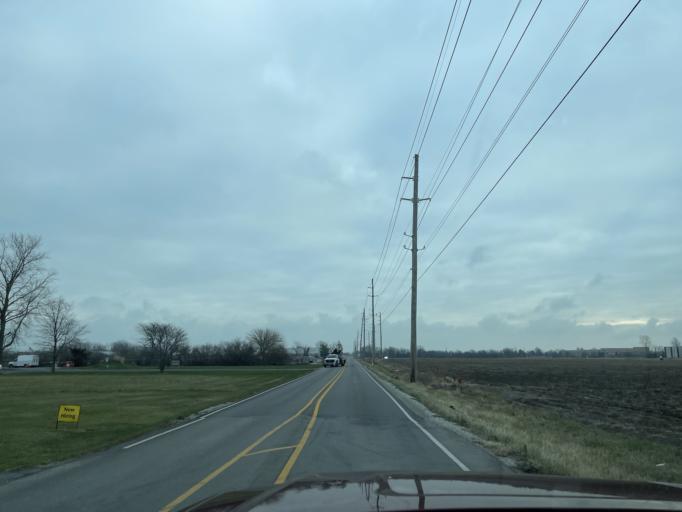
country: US
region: Indiana
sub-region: Boone County
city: Whitestown
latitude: 39.9458
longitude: -86.3686
